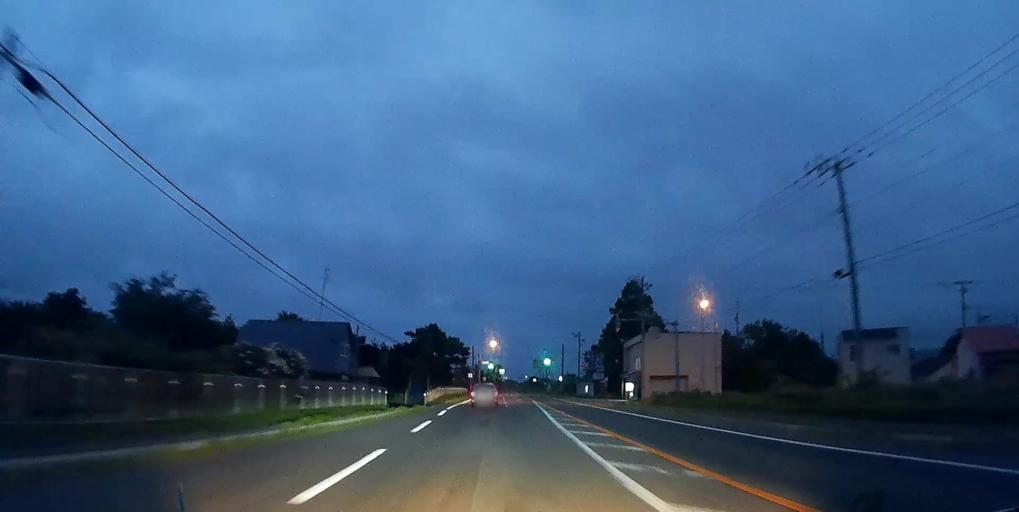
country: JP
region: Hokkaido
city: Nanae
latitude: 42.2189
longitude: 140.3789
